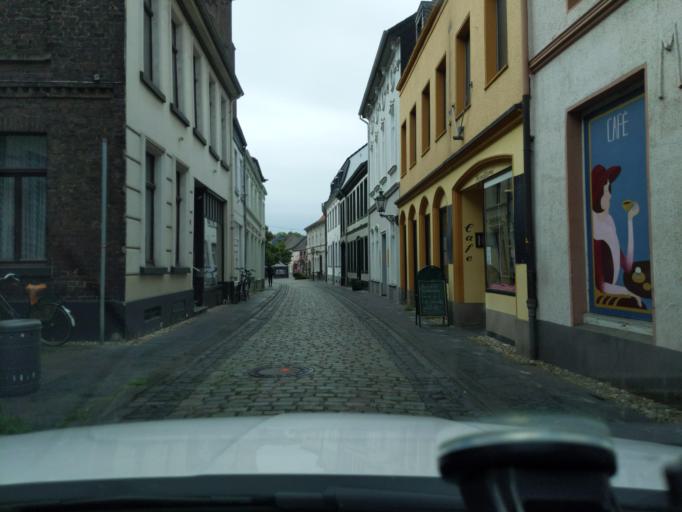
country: DE
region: North Rhine-Westphalia
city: Tonisvorst
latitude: 51.3739
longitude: 6.5097
